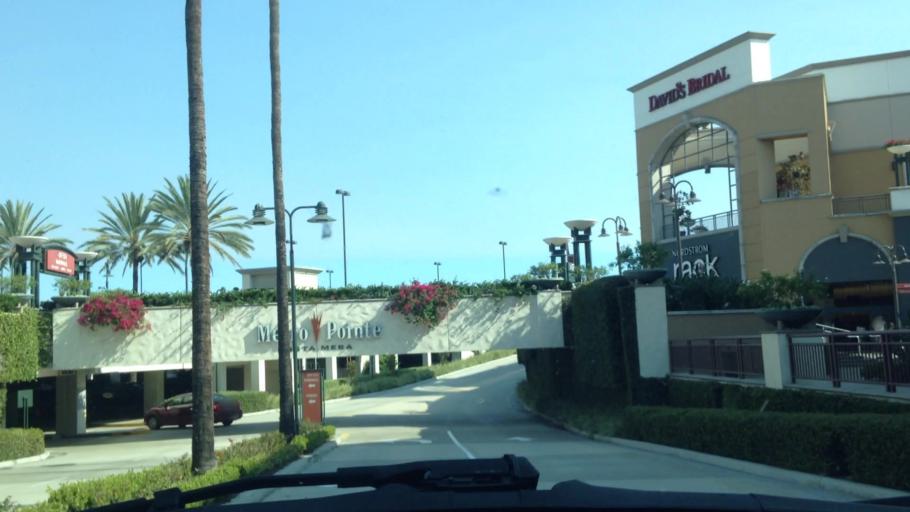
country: US
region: California
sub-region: Orange County
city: Costa Mesa
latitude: 33.6892
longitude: -117.8954
